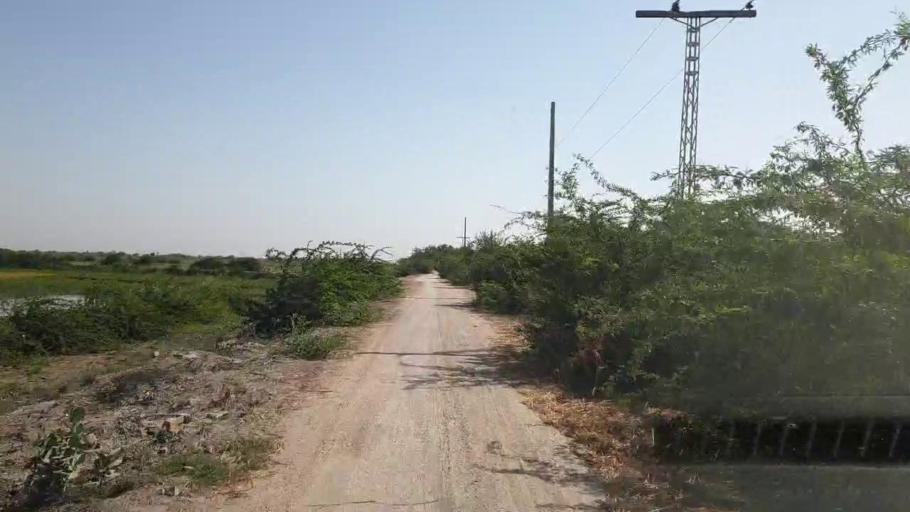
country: PK
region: Sindh
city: Tando Bago
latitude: 24.6432
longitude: 68.9880
